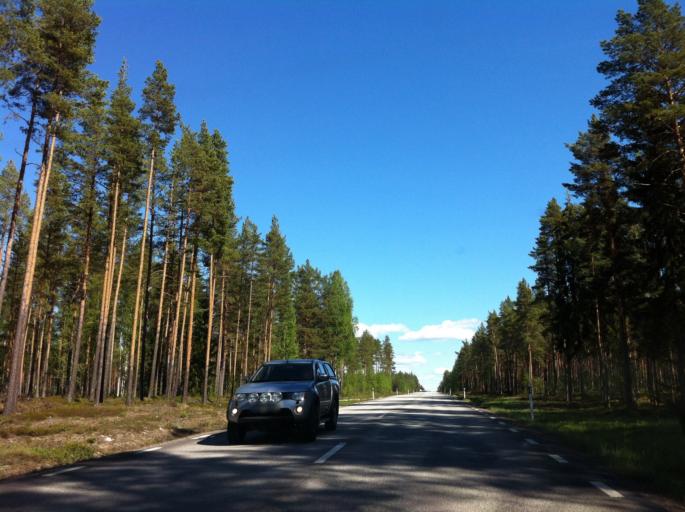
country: SE
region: Dalarna
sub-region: Rattviks Kommun
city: Vikarbyn
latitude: 60.9109
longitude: 14.9066
